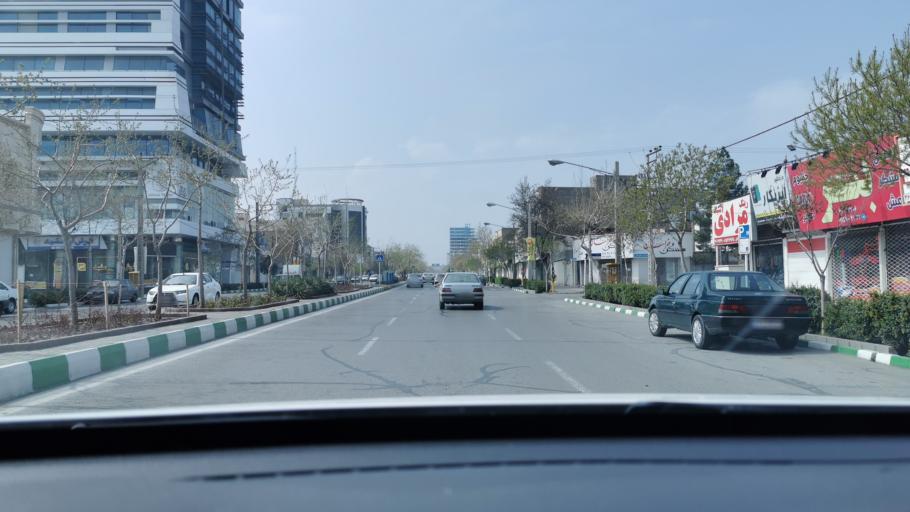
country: IR
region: Razavi Khorasan
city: Mashhad
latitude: 36.3298
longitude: 59.5241
